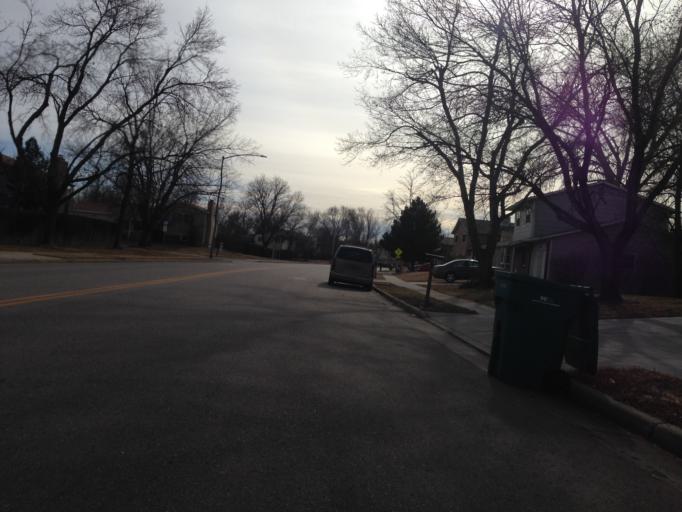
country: US
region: Colorado
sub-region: Adams County
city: Westminster
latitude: 39.8512
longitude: -105.0641
